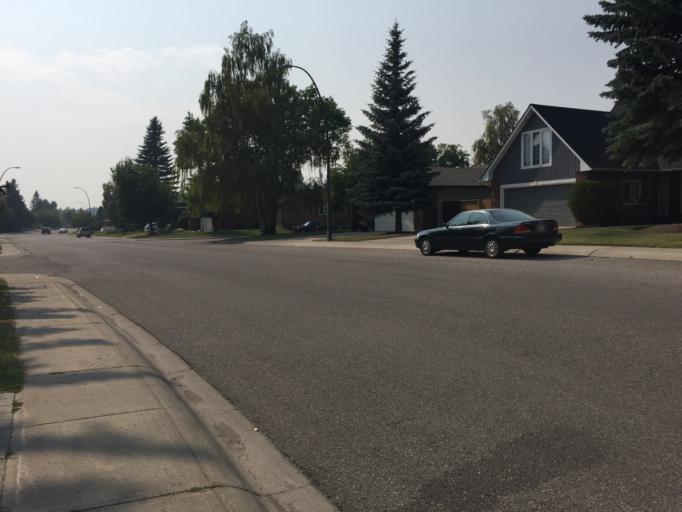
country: CA
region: Alberta
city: Calgary
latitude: 50.9369
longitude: -114.0602
